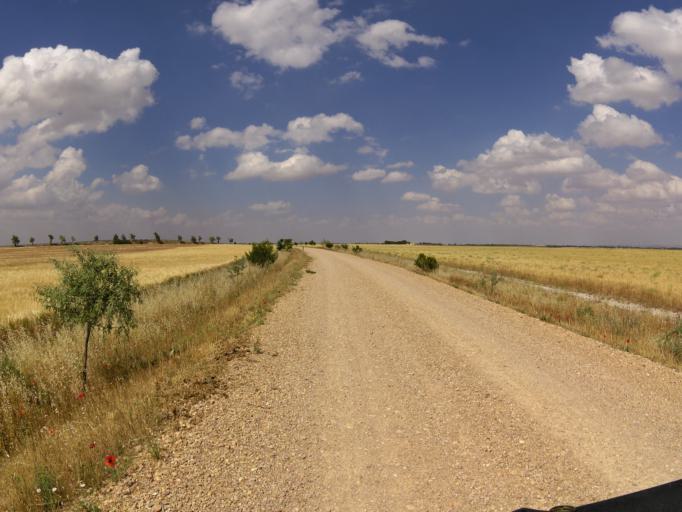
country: ES
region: Castille-La Mancha
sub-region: Provincia de Albacete
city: Albacete
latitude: 38.9415
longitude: -1.9806
